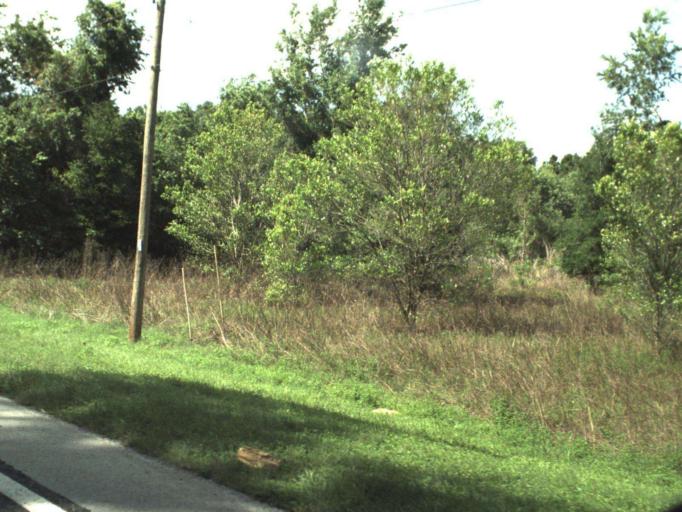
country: US
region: Florida
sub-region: Marion County
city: Belleview
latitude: 29.1030
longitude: -82.0889
